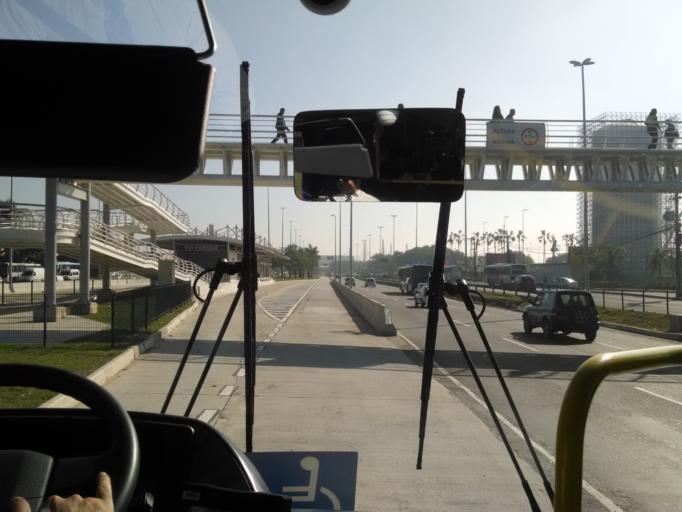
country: BR
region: Rio de Janeiro
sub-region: Rio De Janeiro
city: Rio de Janeiro
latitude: -22.9848
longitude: -43.3658
